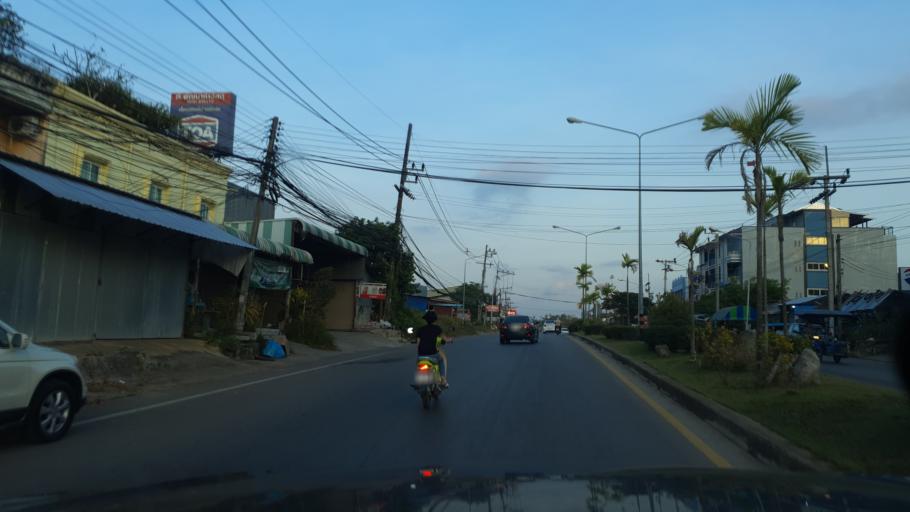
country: TH
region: Phangnga
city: Ban Ao Nang
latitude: 8.0416
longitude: 98.8371
